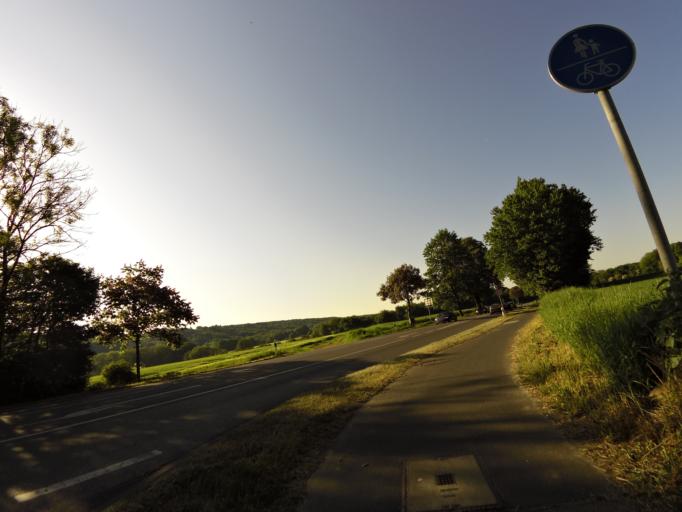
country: DE
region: North Rhine-Westphalia
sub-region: Regierungsbezirk Koln
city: Bonn
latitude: 50.6935
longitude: 7.0711
